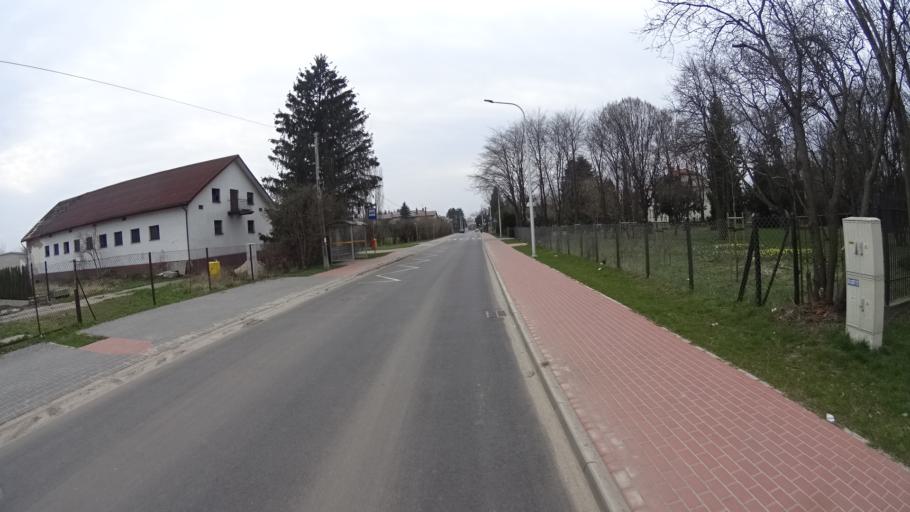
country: PL
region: Masovian Voivodeship
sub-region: Powiat pruszkowski
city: Piastow
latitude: 52.2108
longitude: 20.8438
